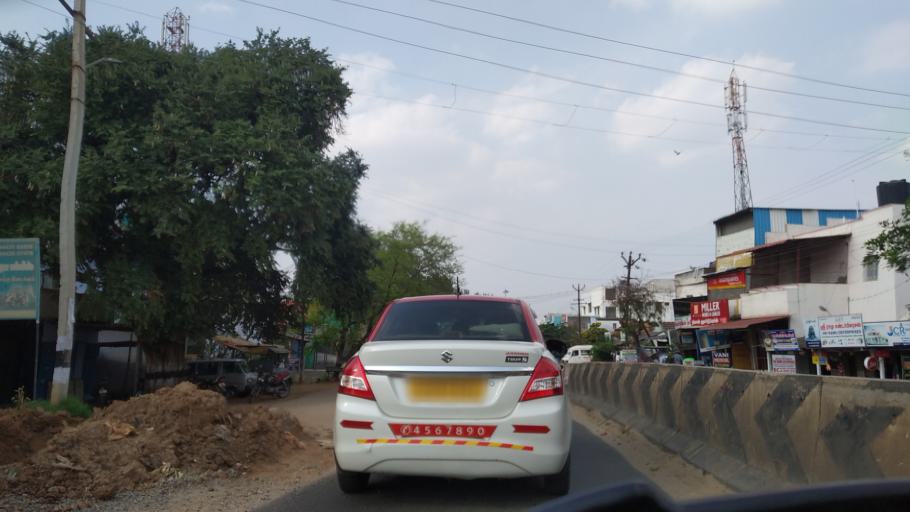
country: IN
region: Tamil Nadu
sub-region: Coimbatore
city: Perur
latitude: 10.9728
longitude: 76.9128
